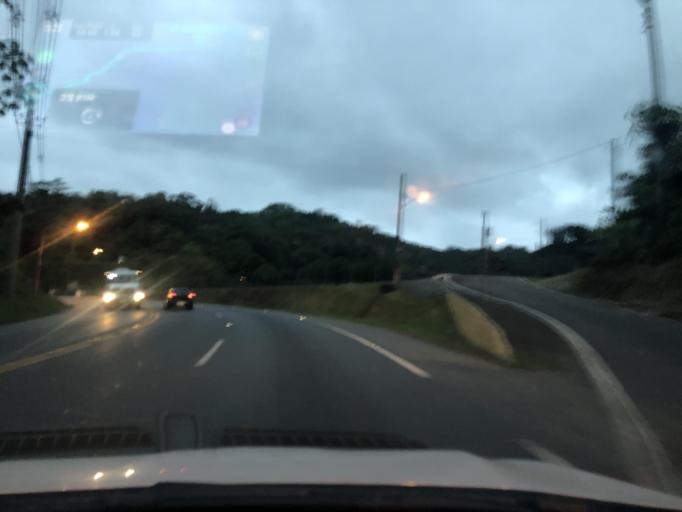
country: BR
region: Santa Catarina
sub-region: Pomerode
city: Pomerode
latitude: -26.7332
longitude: -49.0648
